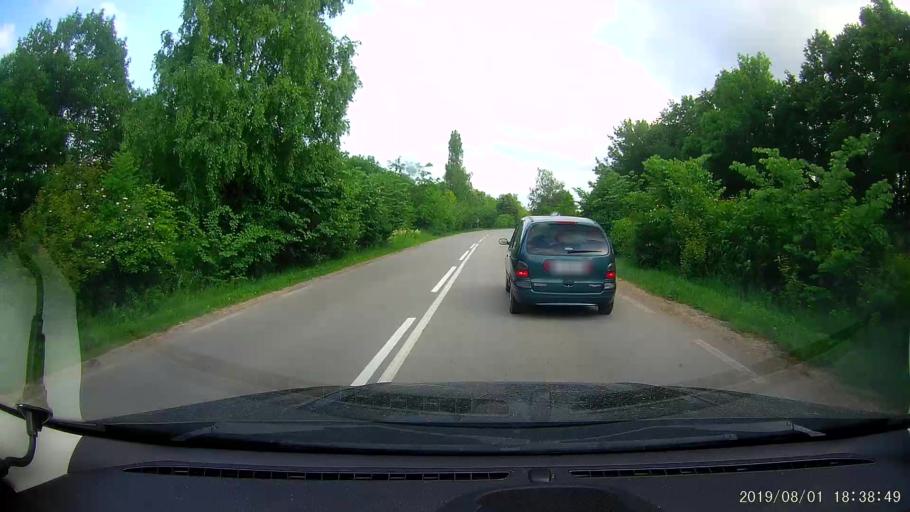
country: BG
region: Shumen
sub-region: Obshtina Khitrino
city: Gara Khitrino
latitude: 43.3972
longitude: 26.9168
